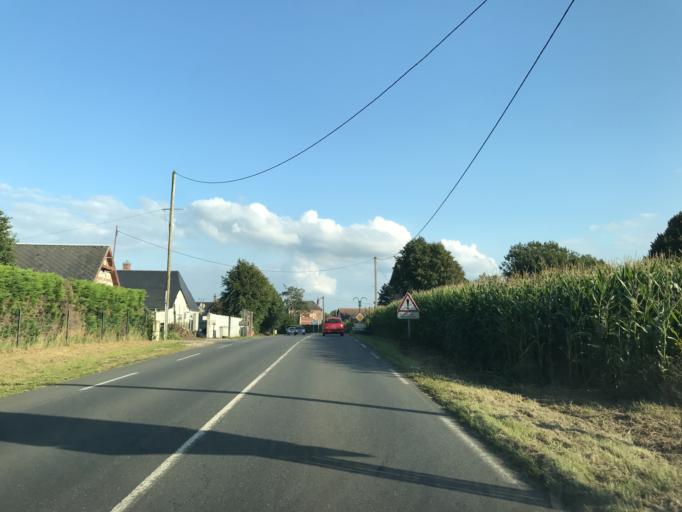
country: FR
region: Haute-Normandie
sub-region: Departement de la Seine-Maritime
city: Beuzeville-la-Grenier
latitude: 49.5972
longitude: 0.4197
